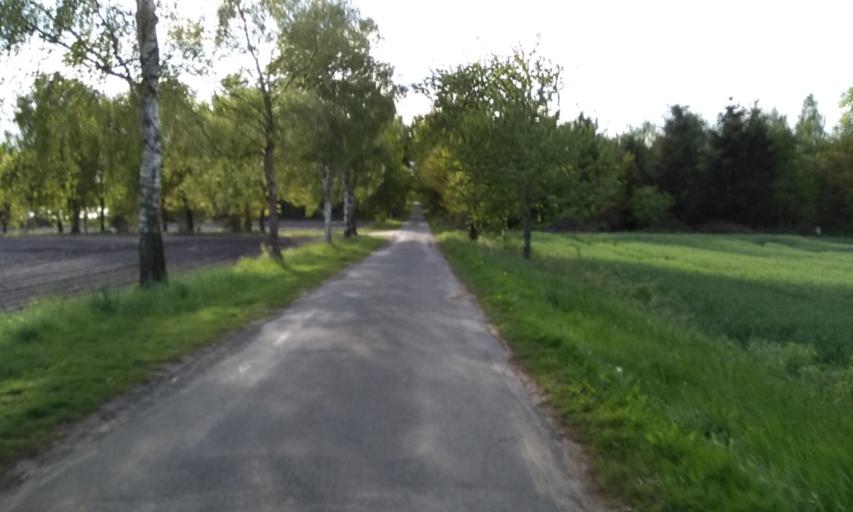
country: DE
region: Lower Saxony
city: Bliedersdorf
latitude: 53.4819
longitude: 9.5602
